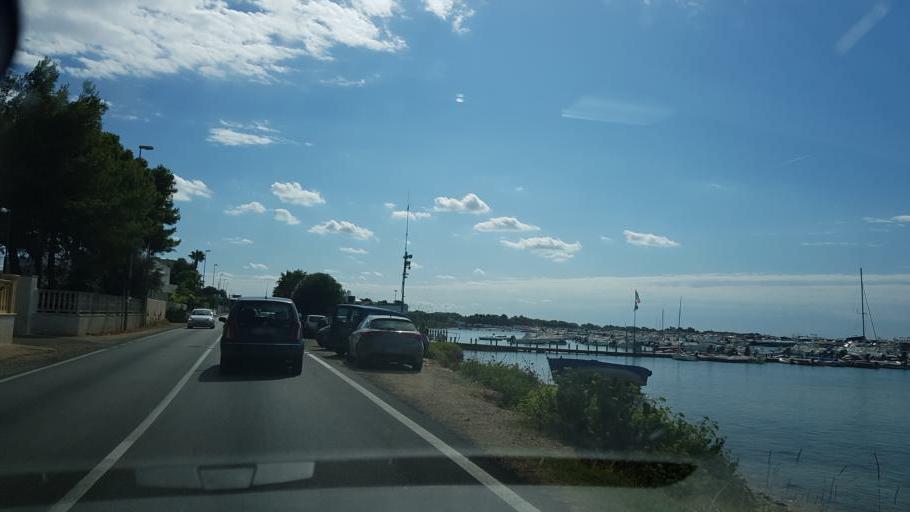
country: IT
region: Apulia
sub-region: Provincia di Lecce
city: Porto Cesareo
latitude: 40.2545
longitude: 17.9059
